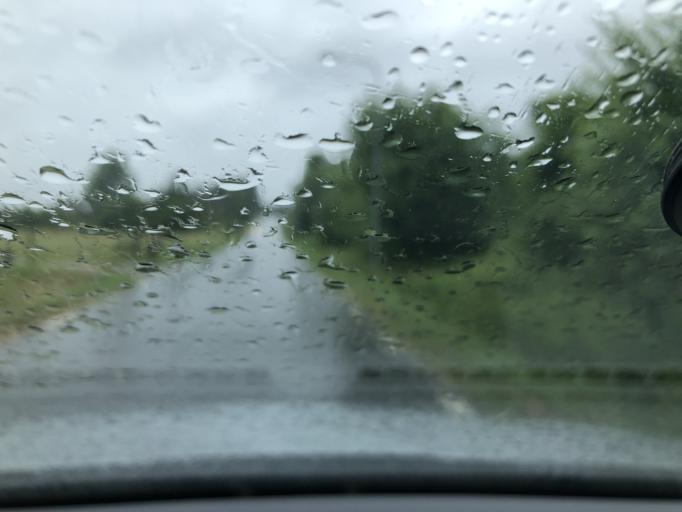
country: SE
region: Blekinge
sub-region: Olofstroms Kommun
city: Jamshog
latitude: 56.1859
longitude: 14.6113
